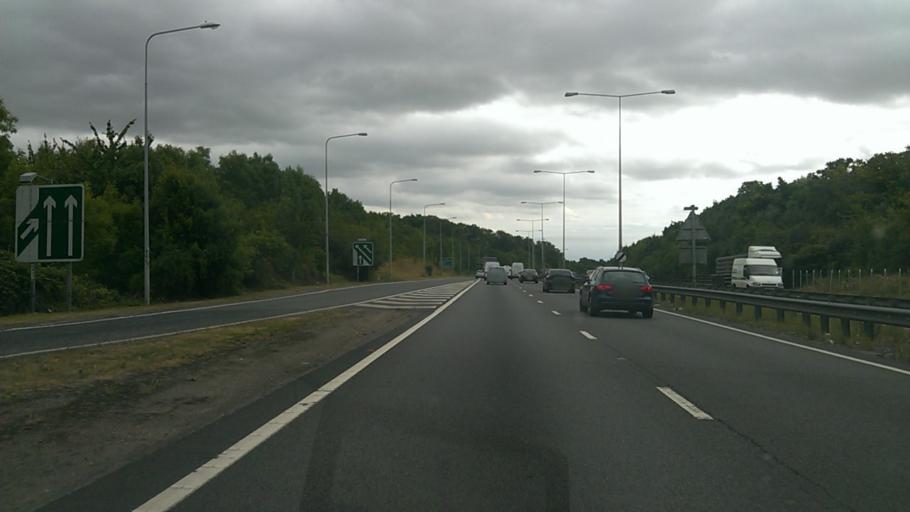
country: GB
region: England
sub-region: Cambridgeshire
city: Brampton
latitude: 52.3370
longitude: -0.2135
